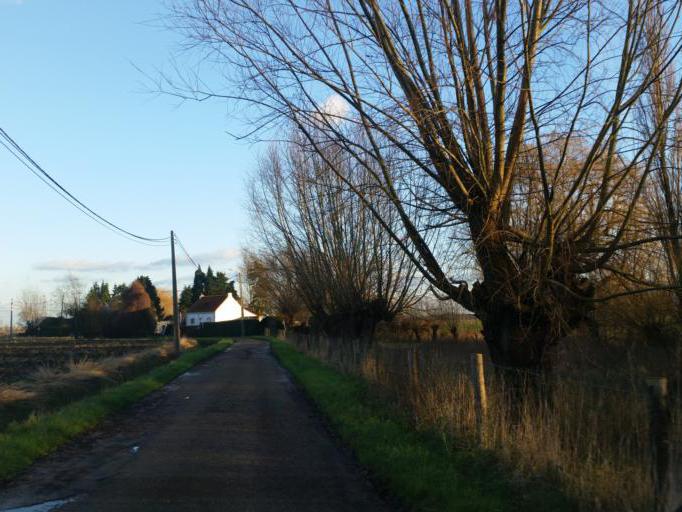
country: BE
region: Flanders
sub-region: Provincie Oost-Vlaanderen
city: Beveren
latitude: 51.3206
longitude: 4.2289
